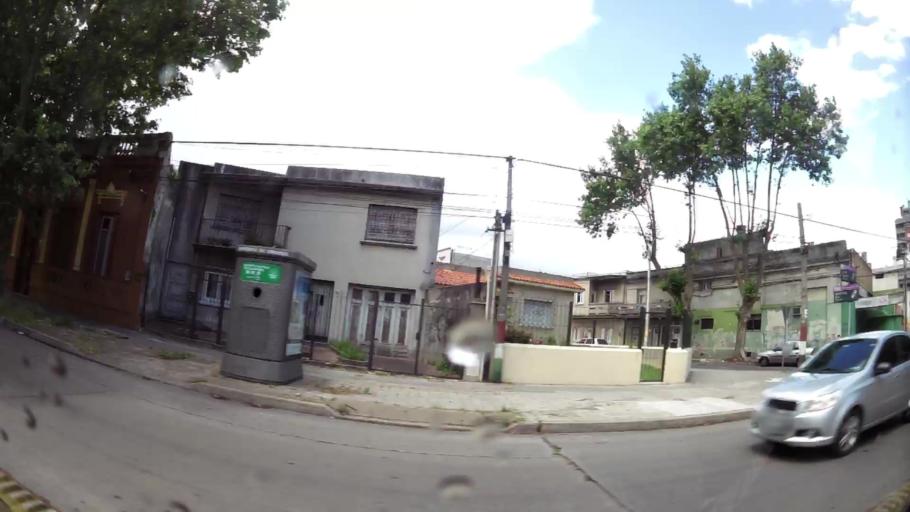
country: UY
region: Montevideo
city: Montevideo
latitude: -34.8699
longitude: -56.1817
